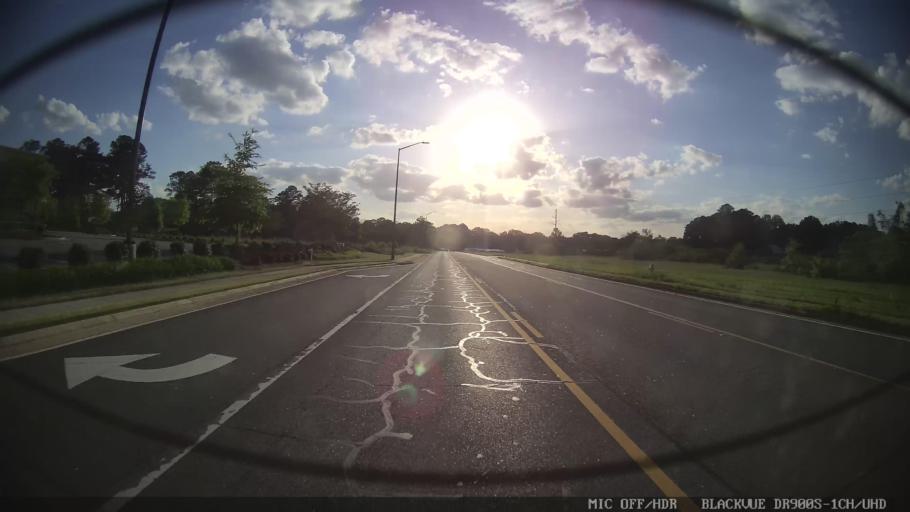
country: US
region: Georgia
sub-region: Bartow County
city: Cartersville
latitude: 34.1863
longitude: -84.7914
